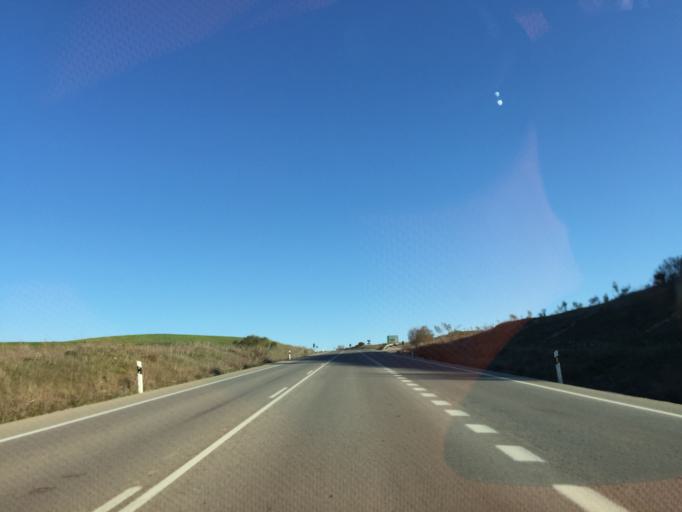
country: ES
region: Andalusia
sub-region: Provincia de Malaga
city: Ardales
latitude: 36.9119
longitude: -4.8418
